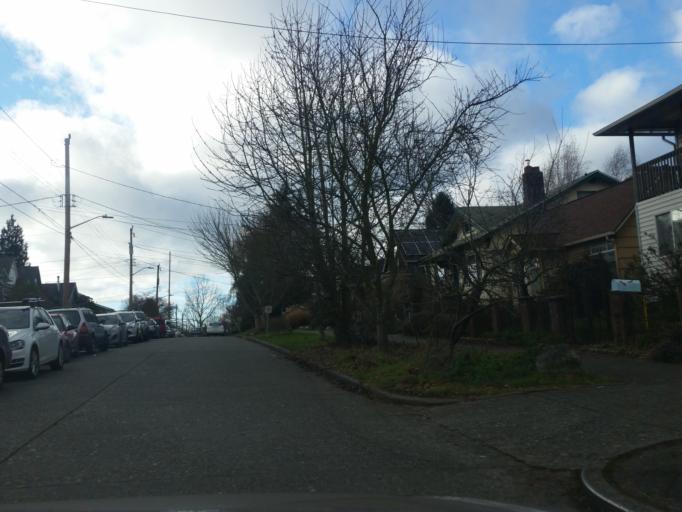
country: US
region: Washington
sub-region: King County
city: Shoreline
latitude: 47.6892
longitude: -122.3557
